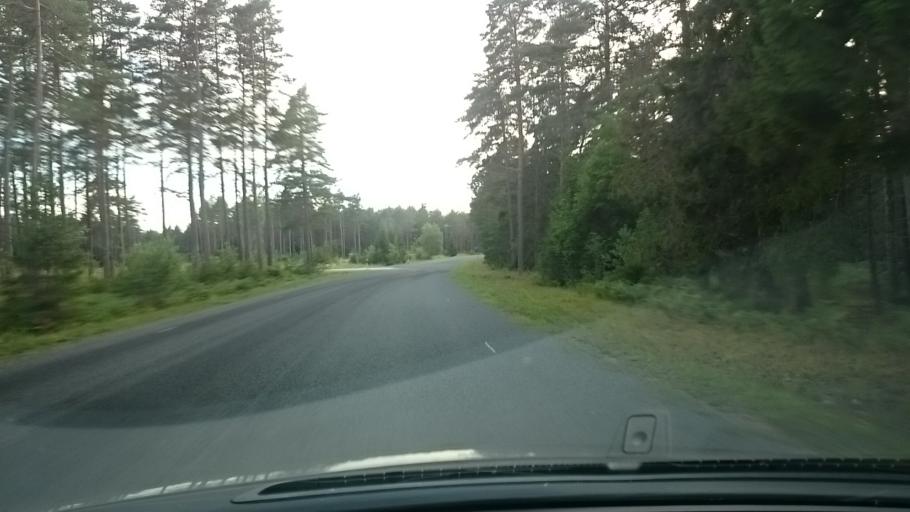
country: EE
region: Saare
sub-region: Kuressaare linn
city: Kuressaare
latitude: 58.4195
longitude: 22.1677
